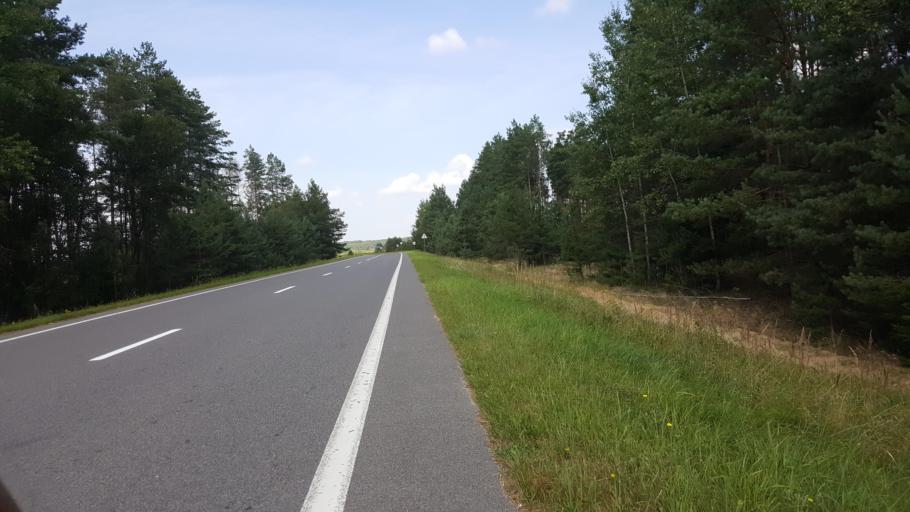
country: BY
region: Brest
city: Kamyanyuki
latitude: 52.5623
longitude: 23.6216
